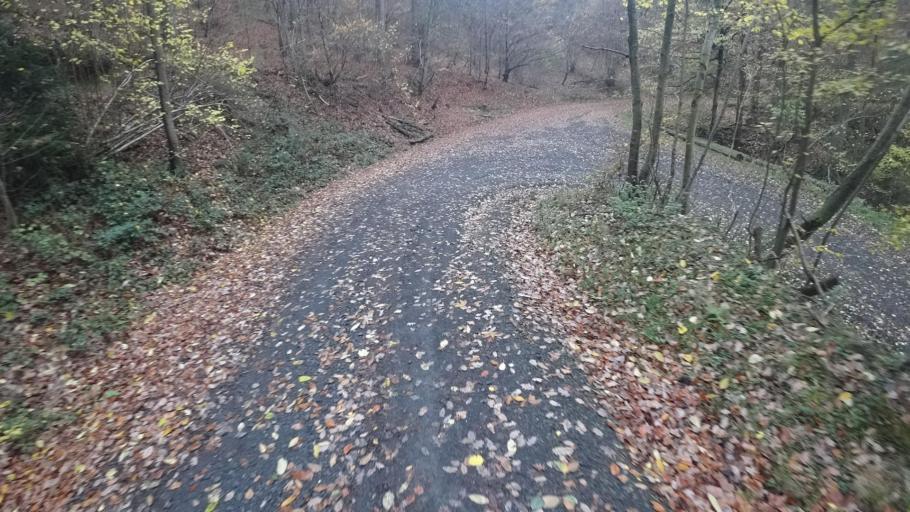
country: DE
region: Rheinland-Pfalz
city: Rech
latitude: 50.5004
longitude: 7.0509
